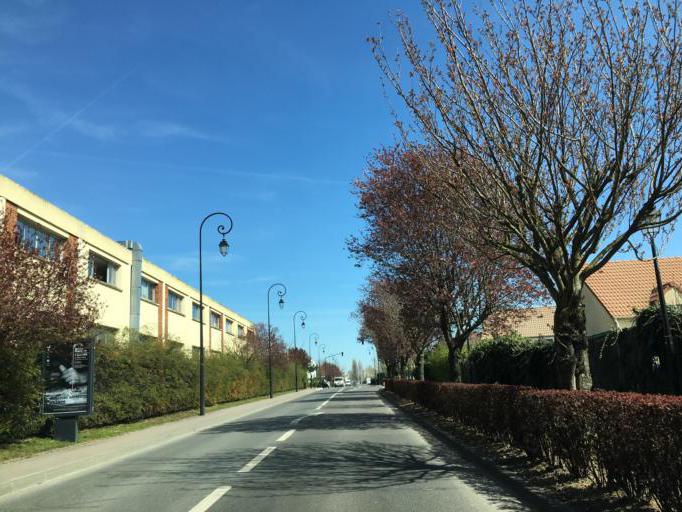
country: FR
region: Ile-de-France
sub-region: Departement de Seine-Saint-Denis
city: Neuilly-Plaisance
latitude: 48.8637
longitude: 2.5153
